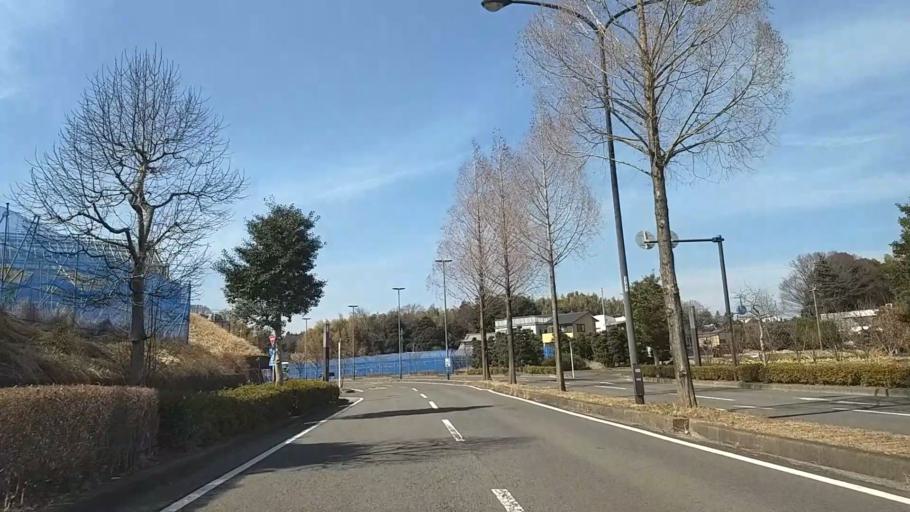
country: JP
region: Kanagawa
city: Fujisawa
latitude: 35.3928
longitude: 139.4245
